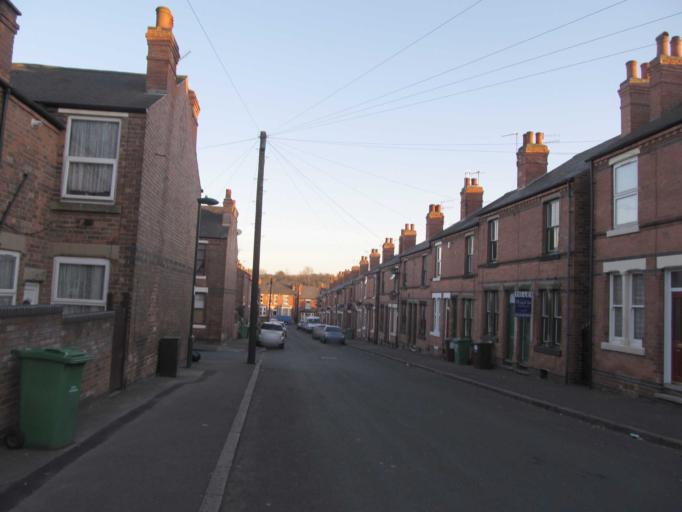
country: GB
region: England
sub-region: Nottingham
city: Nottingham
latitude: 52.9699
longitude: -1.1644
